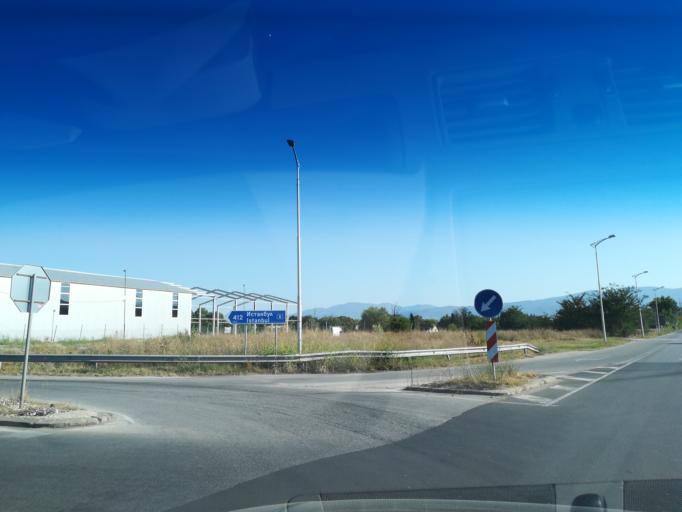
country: BG
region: Plovdiv
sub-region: Obshtina Plovdiv
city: Plovdiv
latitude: 42.1467
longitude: 24.8060
